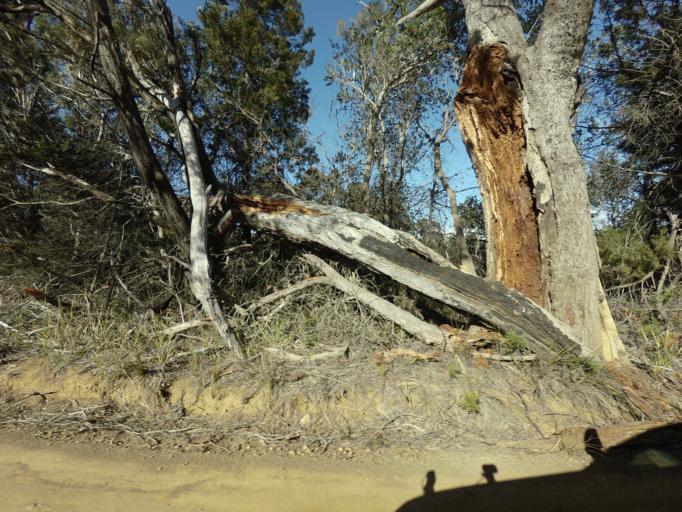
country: AU
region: Tasmania
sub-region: Sorell
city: Sorell
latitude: -42.3555
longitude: 147.9656
